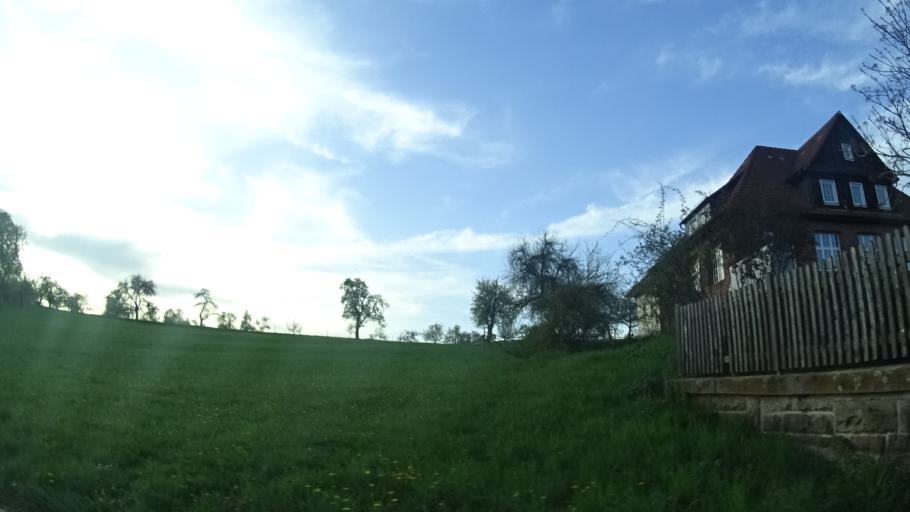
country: DE
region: Baden-Wuerttemberg
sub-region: Karlsruhe Region
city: Fahrenbach
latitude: 49.4735
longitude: 9.1478
